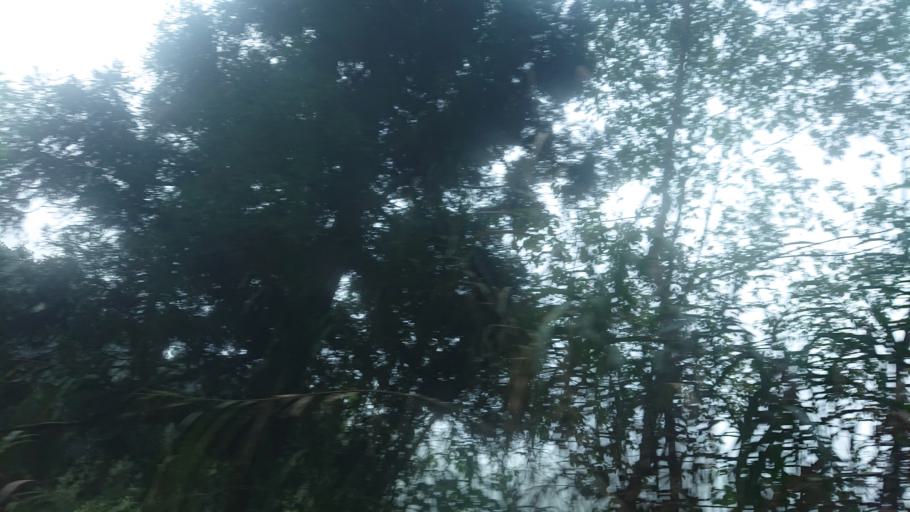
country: TW
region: Taiwan
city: Lugu
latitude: 23.6238
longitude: 120.7185
